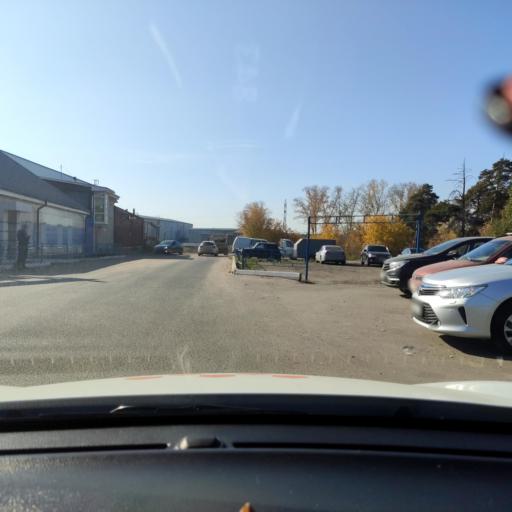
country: RU
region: Tatarstan
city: Staroye Arakchino
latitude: 55.8367
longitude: 49.0278
